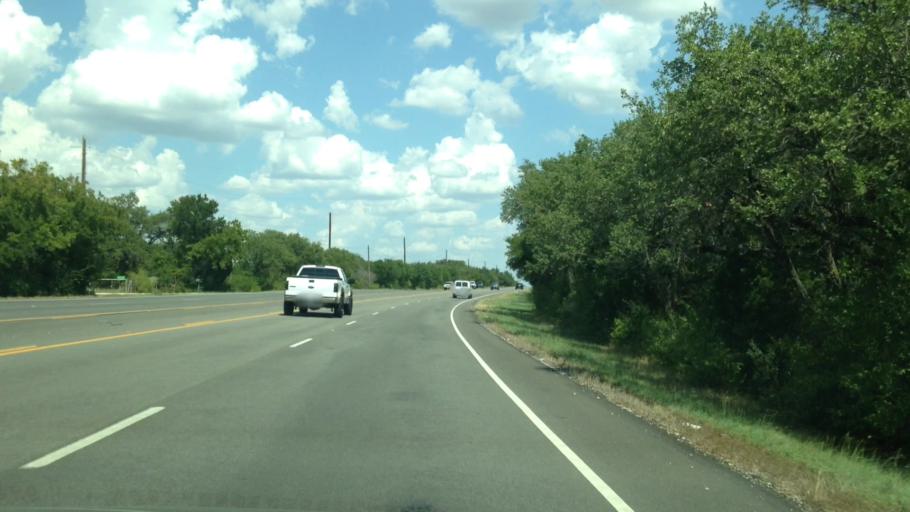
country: US
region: Texas
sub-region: Williamson County
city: Georgetown
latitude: 30.6345
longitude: -97.7268
